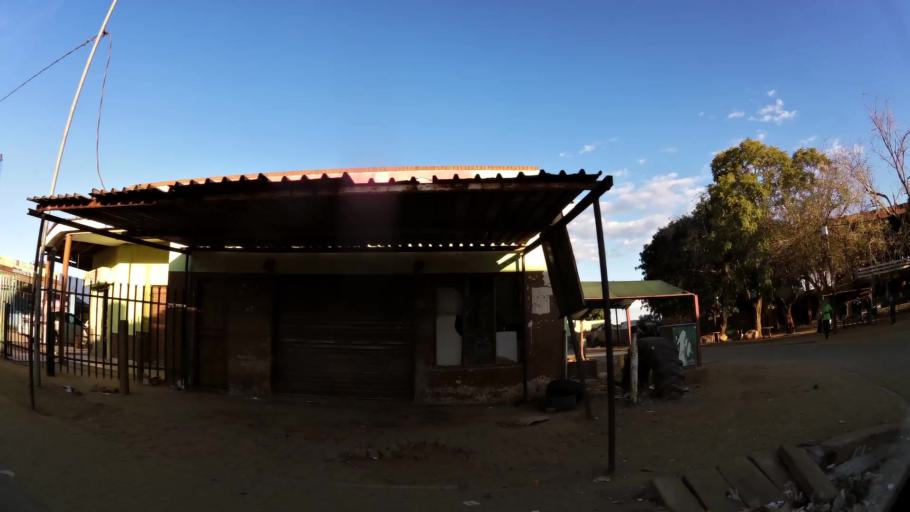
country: ZA
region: Limpopo
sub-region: Waterberg District Municipality
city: Mokopane
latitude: -24.1492
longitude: 28.9807
